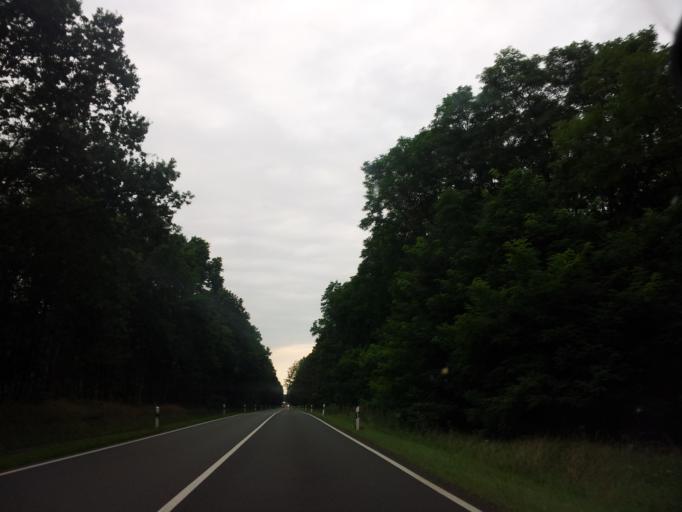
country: DE
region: Brandenburg
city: Treuenbrietzen
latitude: 52.0468
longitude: 12.9167
